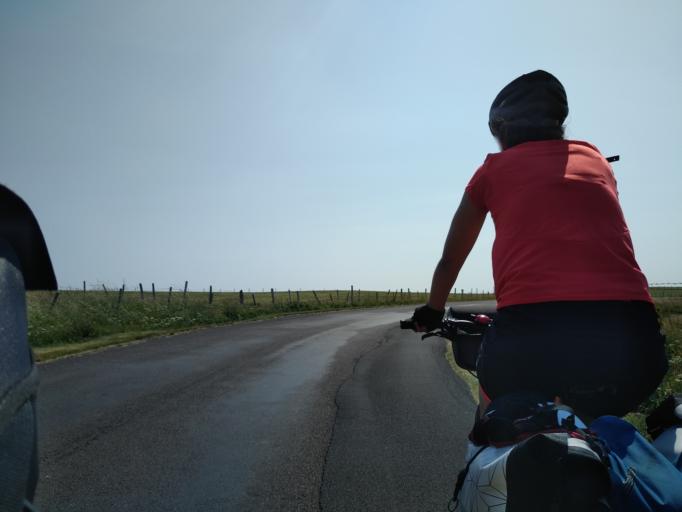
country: FR
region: Auvergne
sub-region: Departement du Puy-de-Dome
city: Mont-Dore
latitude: 45.5641
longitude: 2.8364
